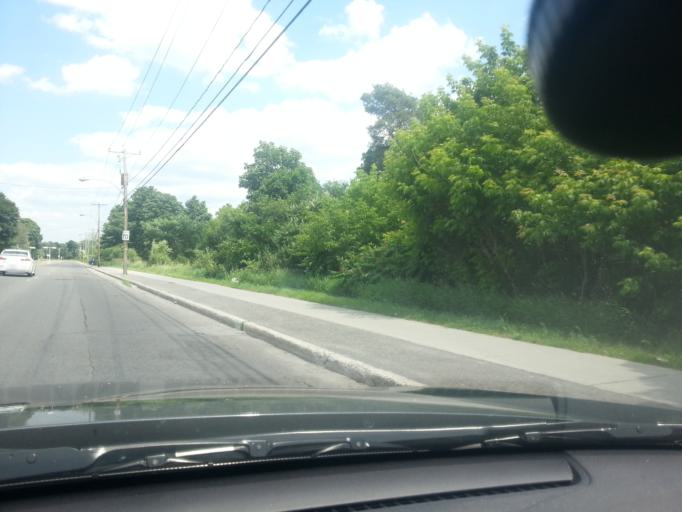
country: CA
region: Ontario
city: Bells Corners
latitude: 45.3964
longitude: -75.8219
